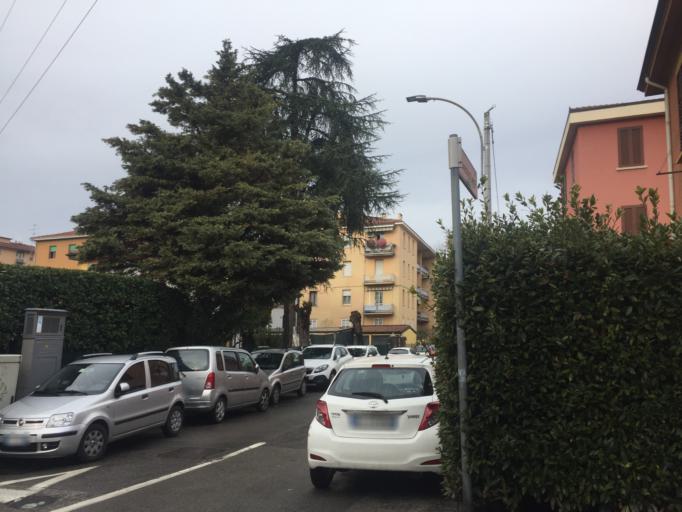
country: IT
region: Emilia-Romagna
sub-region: Provincia di Bologna
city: Casalecchio di Reno
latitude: 44.5069
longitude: 11.2969
